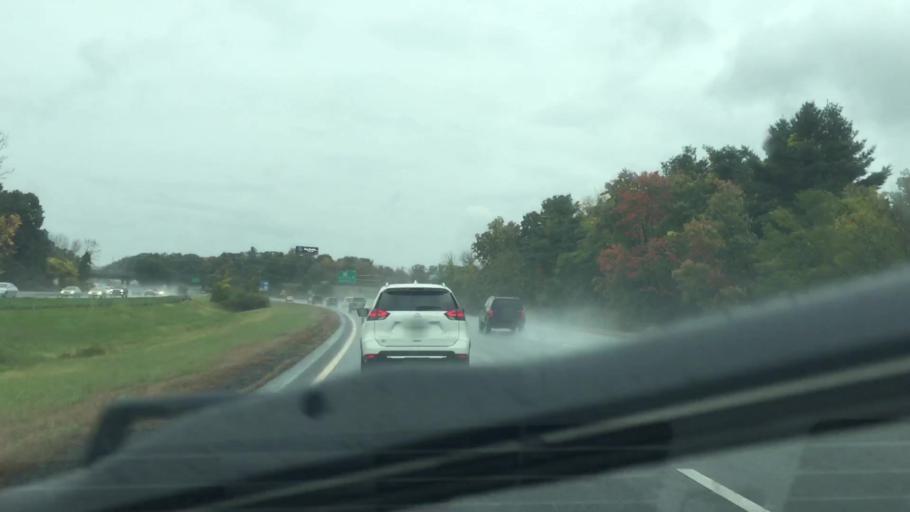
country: US
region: Massachusetts
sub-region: Essex County
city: Haverhill
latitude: 42.7572
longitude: -71.1241
